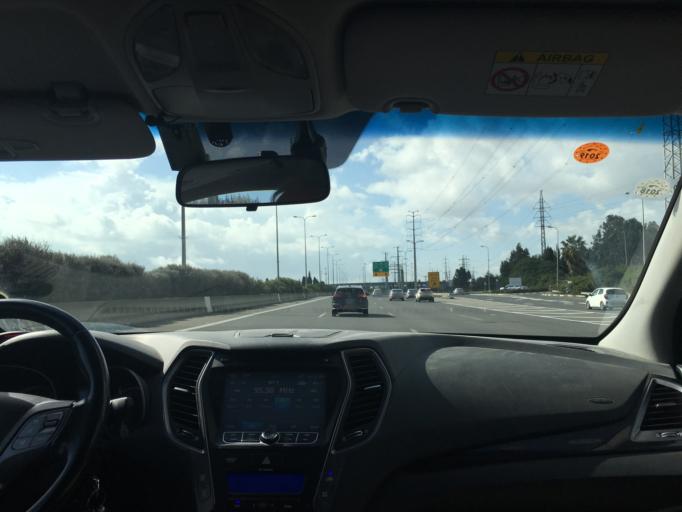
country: IL
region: Tel Aviv
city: Azor
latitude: 32.0265
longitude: 34.8270
